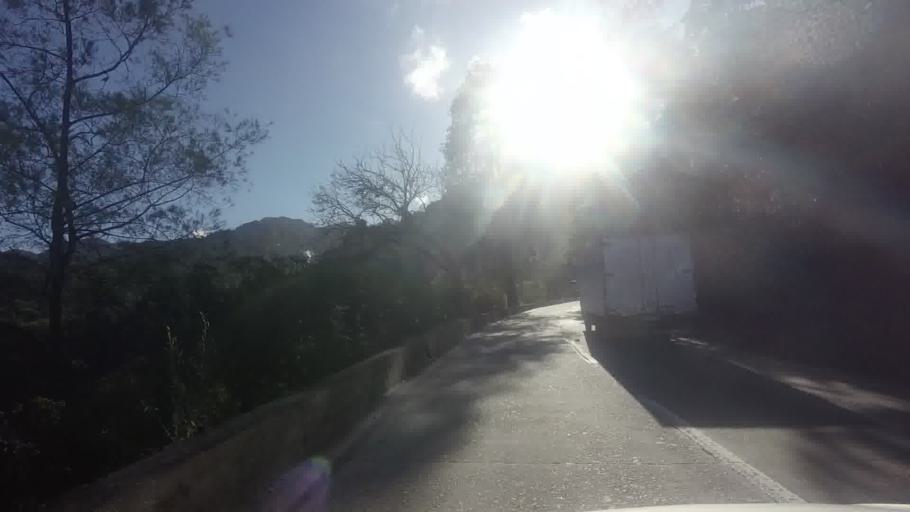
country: BR
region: Rio de Janeiro
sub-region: Petropolis
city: Petropolis
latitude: -22.5649
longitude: -43.2386
